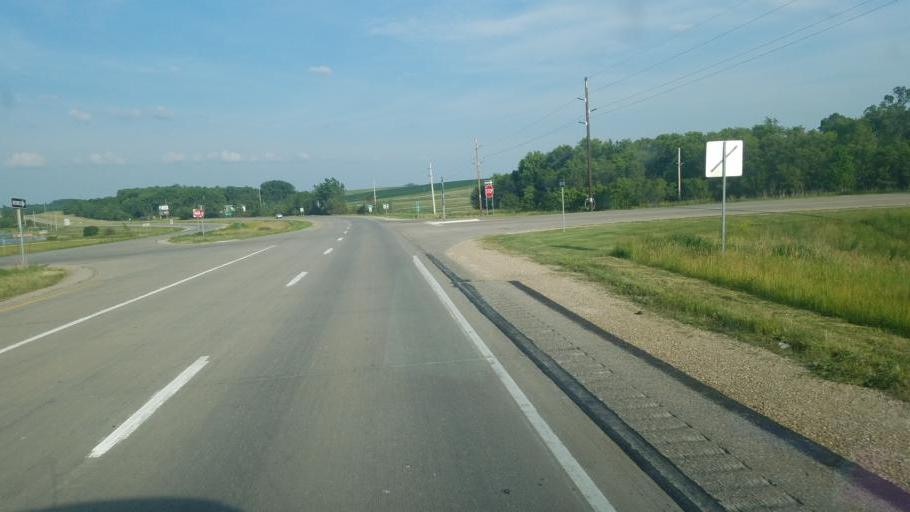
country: US
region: Iowa
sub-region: Marshall County
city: Marshalltown
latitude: 42.0076
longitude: -92.7680
